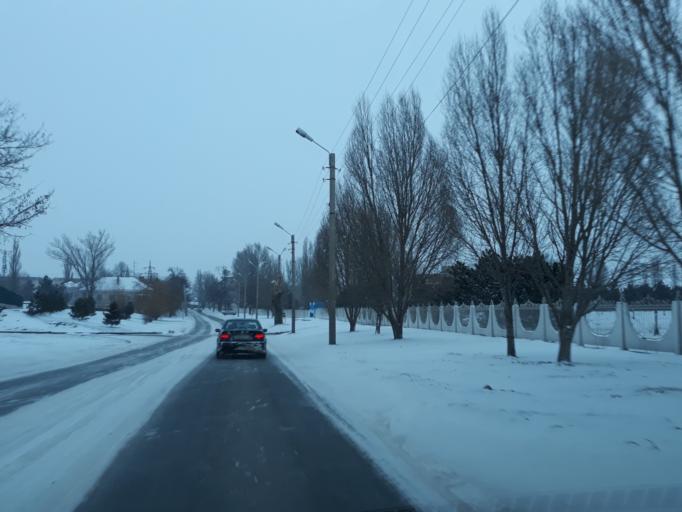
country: RU
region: Rostov
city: Taganrog
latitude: 47.2492
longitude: 38.9332
